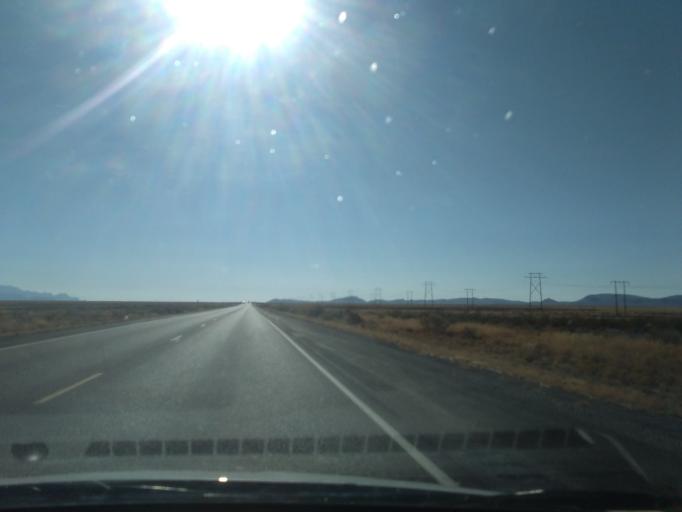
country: US
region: New Mexico
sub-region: Luna County
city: Deming
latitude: 32.4850
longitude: -107.5247
